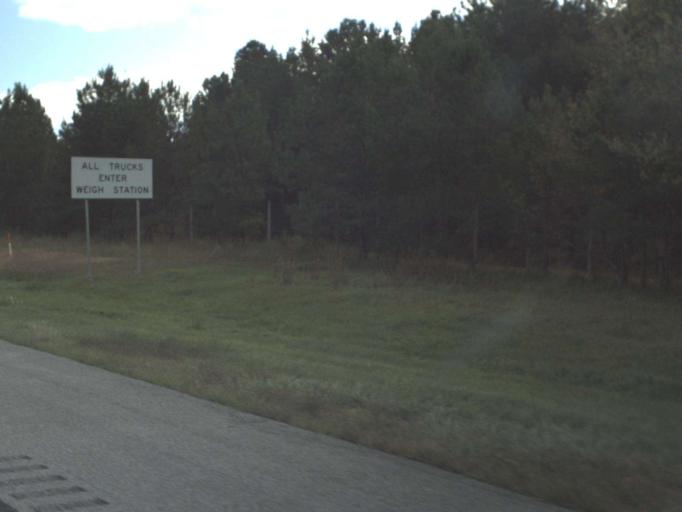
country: US
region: Florida
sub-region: Jackson County
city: Sneads
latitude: 30.6440
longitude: -85.0063
